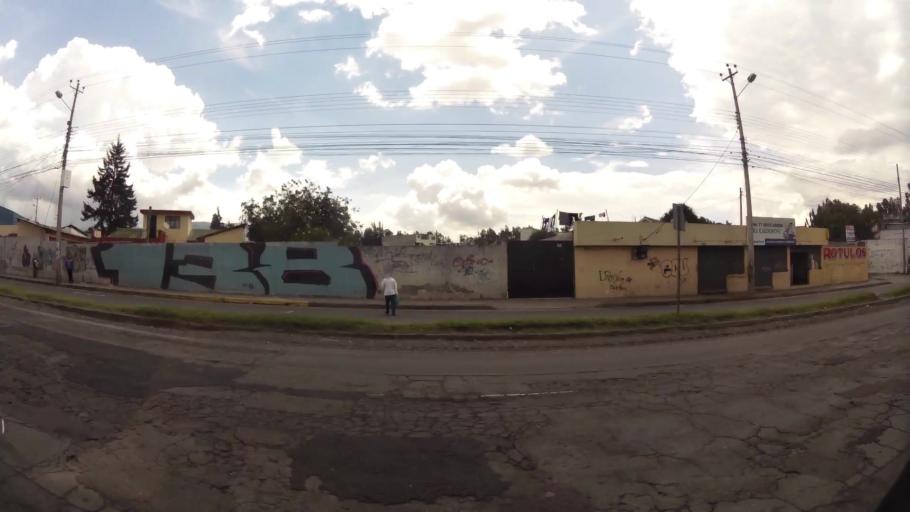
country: EC
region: Pichincha
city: Quito
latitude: -0.1057
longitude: -78.4338
